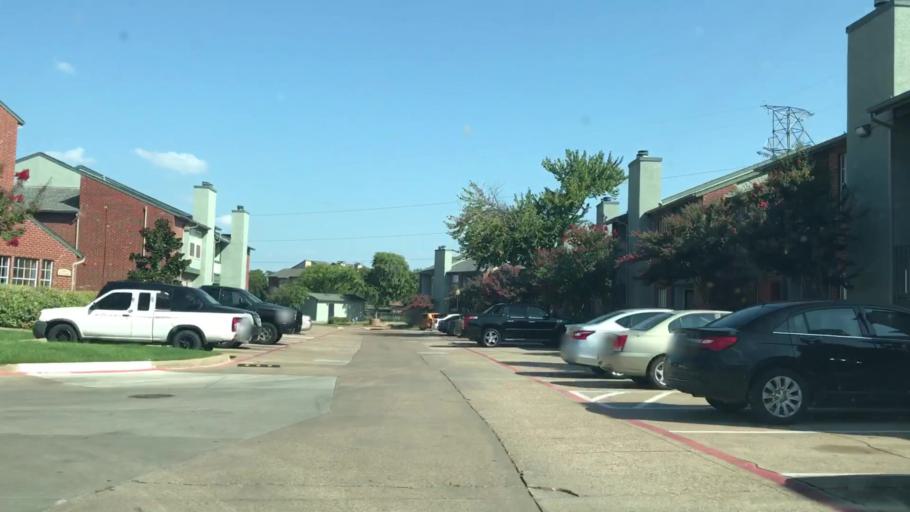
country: US
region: Texas
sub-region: Dallas County
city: Mesquite
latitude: 32.8187
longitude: -96.6354
